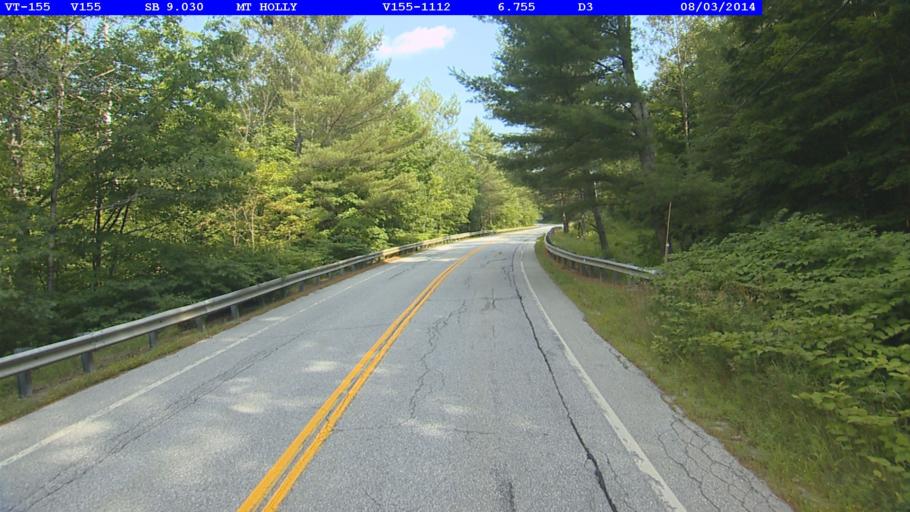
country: US
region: Vermont
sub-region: Rutland County
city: Rutland
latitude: 43.4393
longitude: -72.8616
